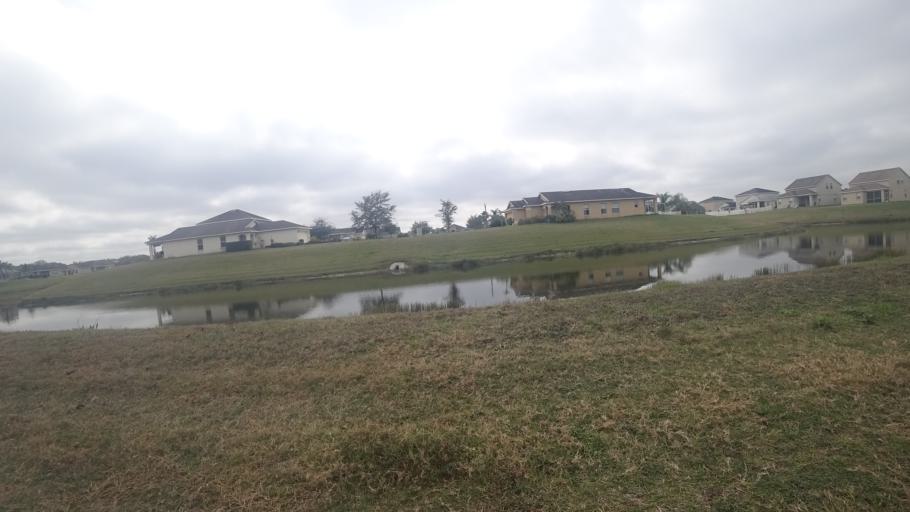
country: US
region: Florida
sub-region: Manatee County
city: Ellenton
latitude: 27.5794
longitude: -82.5086
